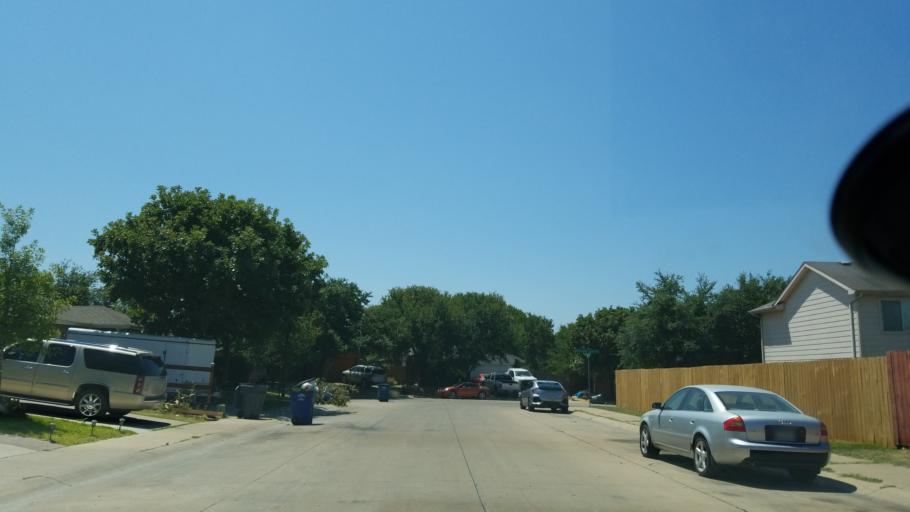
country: US
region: Texas
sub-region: Dallas County
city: Cockrell Hill
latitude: 32.7379
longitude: -96.8945
